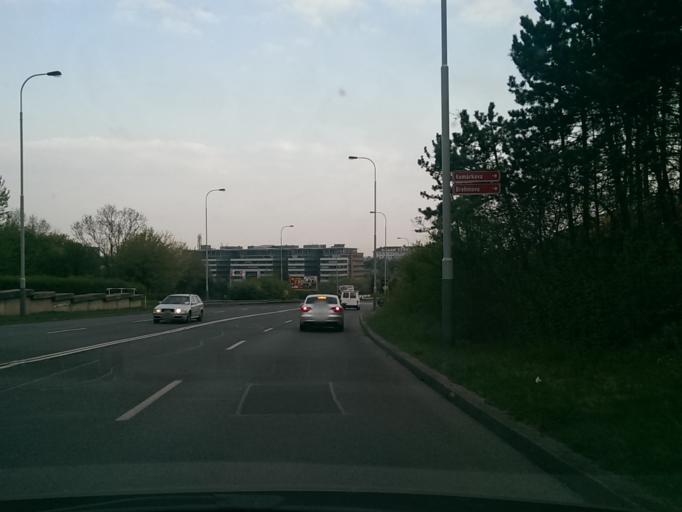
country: CZ
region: Central Bohemia
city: Vestec
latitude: 50.0355
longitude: 14.4800
